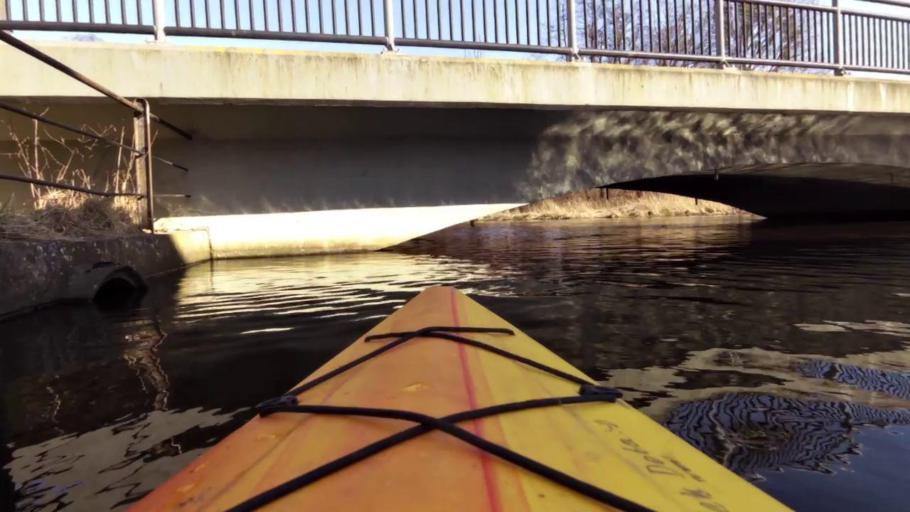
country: PL
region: West Pomeranian Voivodeship
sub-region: Powiat lobeski
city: Resko
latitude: 53.7714
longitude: 15.4036
